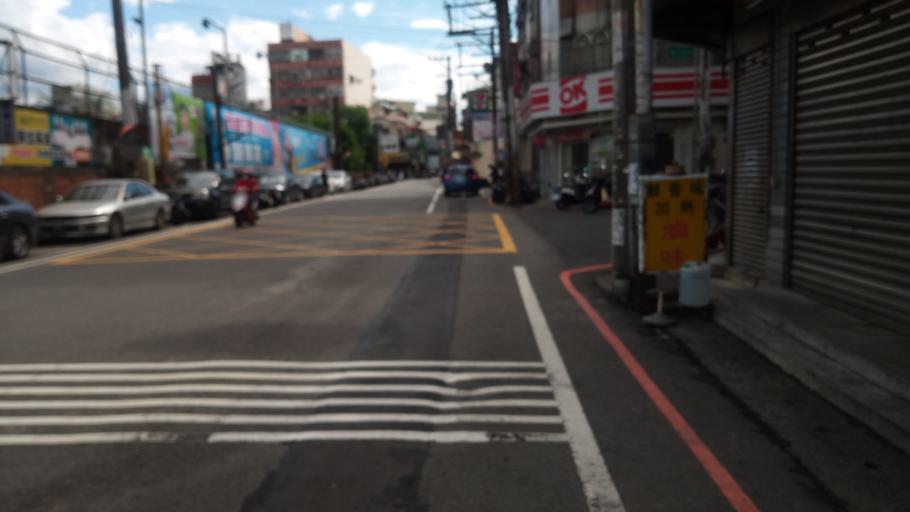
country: TW
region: Taiwan
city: Daxi
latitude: 24.9361
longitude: 121.2495
